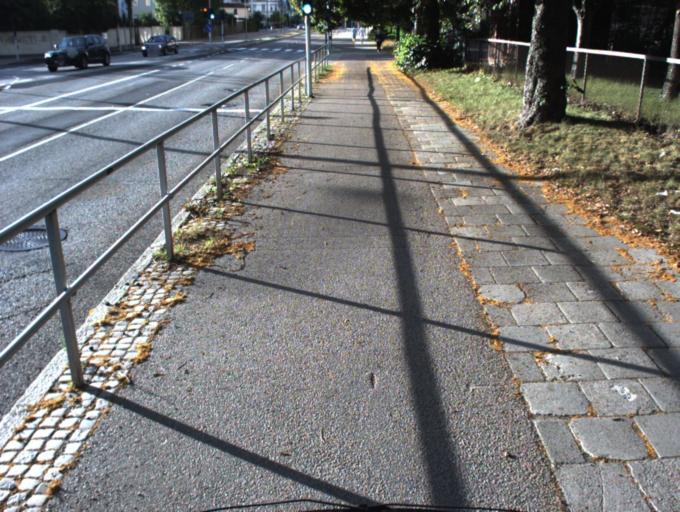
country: SE
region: Skane
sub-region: Helsingborg
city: Helsingborg
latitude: 56.0471
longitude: 12.7072
